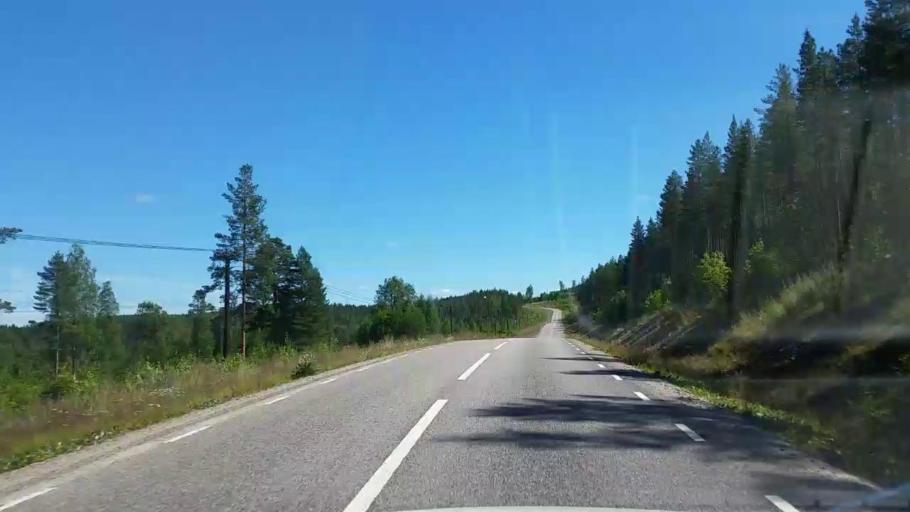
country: SE
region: Gaevleborg
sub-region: Ovanakers Kommun
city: Edsbyn
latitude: 61.5856
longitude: 15.6418
